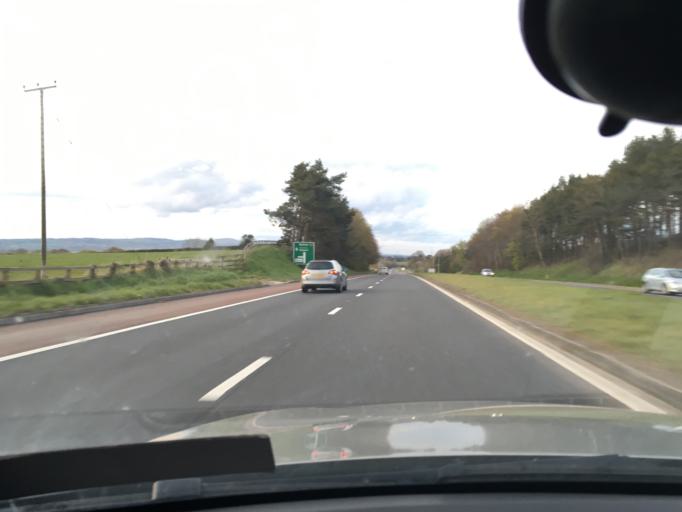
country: GB
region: Northern Ireland
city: Hillsborough
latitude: 54.4608
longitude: -6.0976
